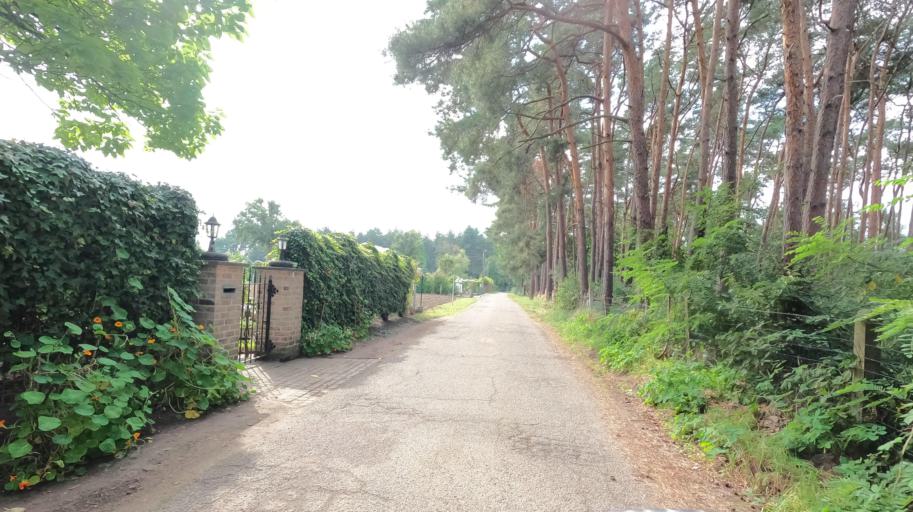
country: BE
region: Flanders
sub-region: Provincie Vlaams-Brabant
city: Keerbergen
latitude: 51.0237
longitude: 4.6726
